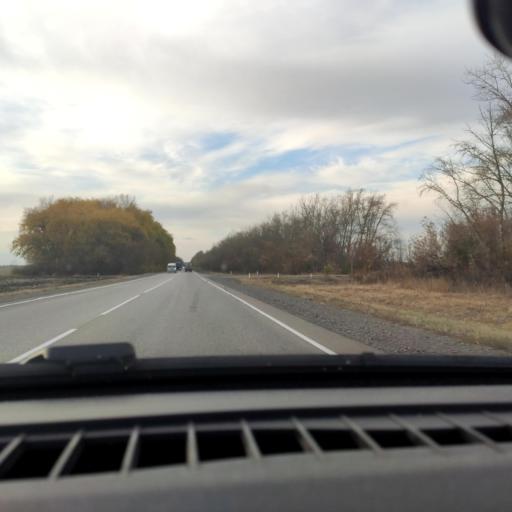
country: RU
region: Voronezj
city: Ostrogozhsk
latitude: 50.9545
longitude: 39.0387
